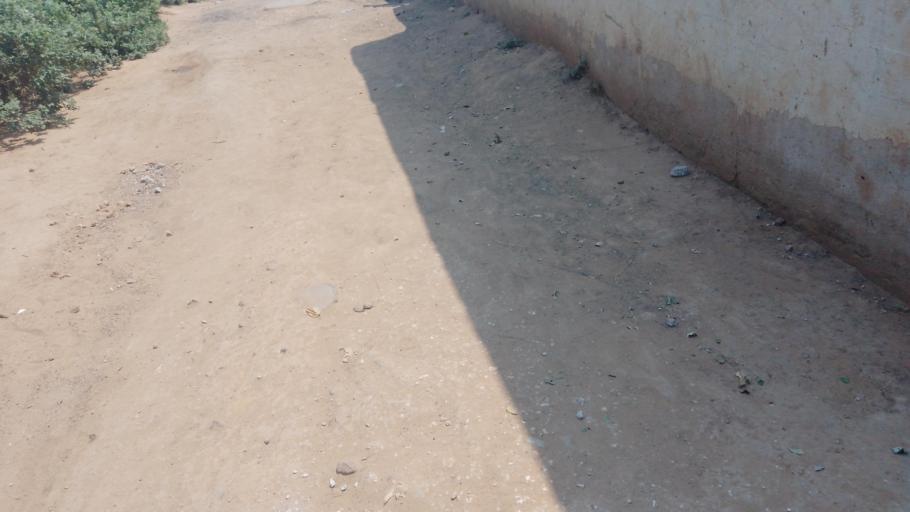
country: ZM
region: Lusaka
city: Lusaka
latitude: -15.3951
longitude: 28.3768
